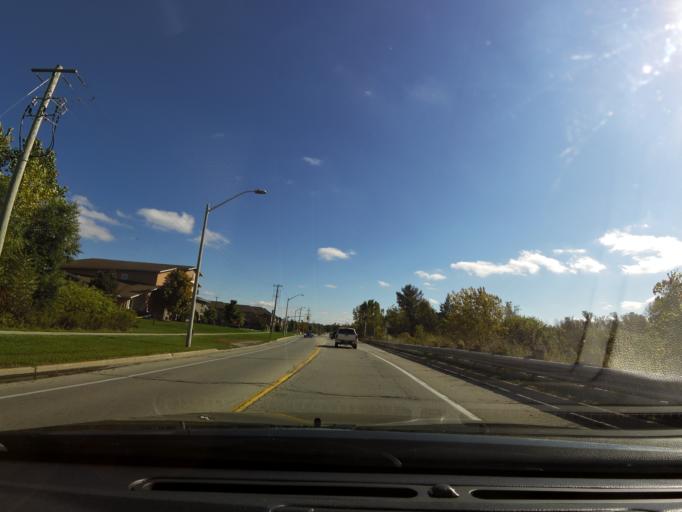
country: CA
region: Ontario
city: Ancaster
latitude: 43.2251
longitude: -79.9356
